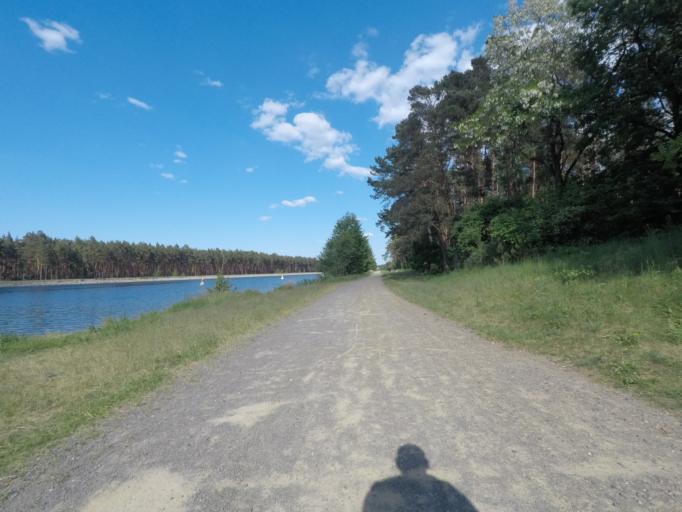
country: DE
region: Brandenburg
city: Eberswalde
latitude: 52.8539
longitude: 13.8130
